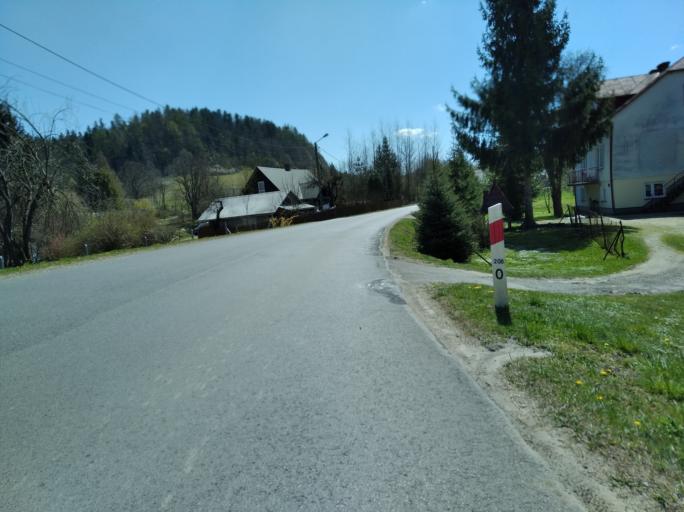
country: PL
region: Subcarpathian Voivodeship
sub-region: Powiat brzozowski
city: Dydnia
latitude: 49.6870
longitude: 22.1874
